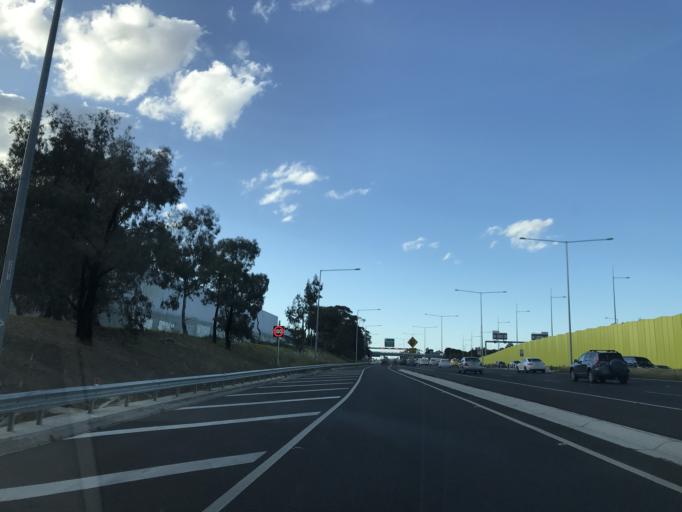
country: AU
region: Victoria
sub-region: Moreland
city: Gowanbrae
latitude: -37.7028
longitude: 144.8885
